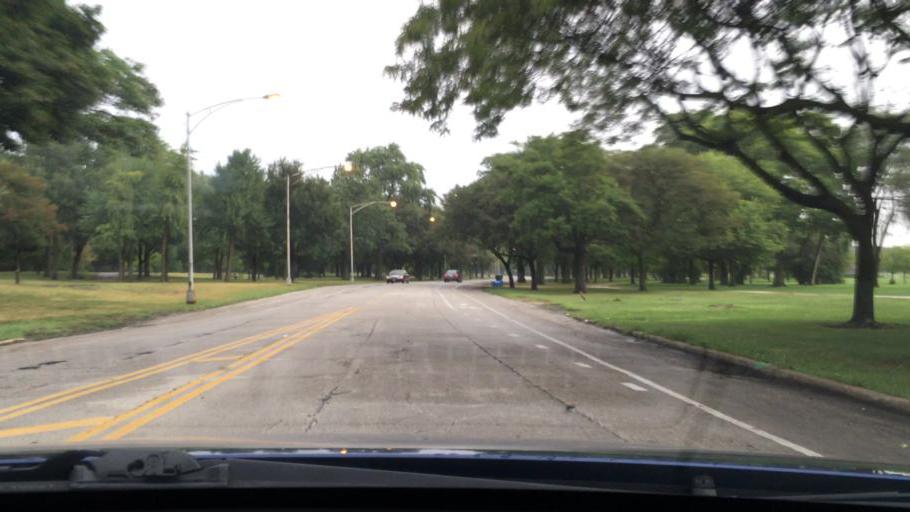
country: US
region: Illinois
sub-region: Cook County
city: Chicago
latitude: 41.7966
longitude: -87.6153
